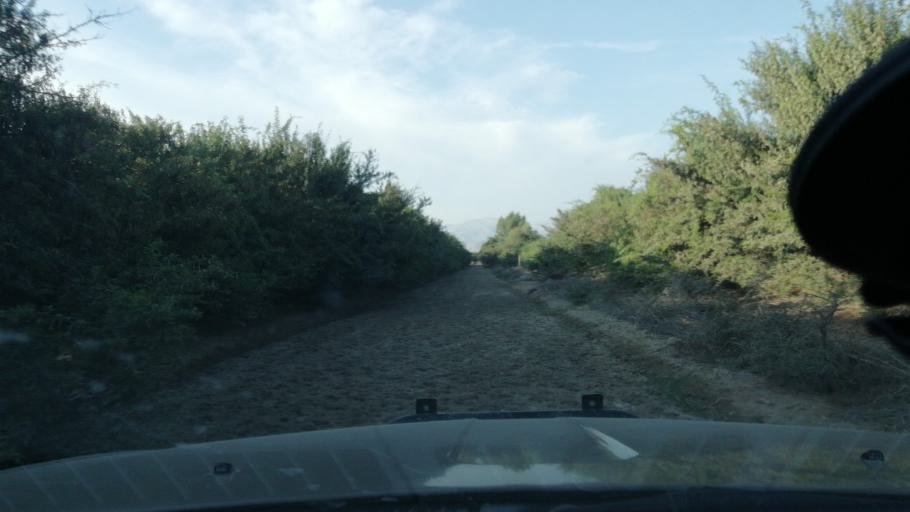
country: PE
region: Ica
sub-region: Provincia de Chincha
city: San Pedro
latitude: -13.3491
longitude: -76.1624
